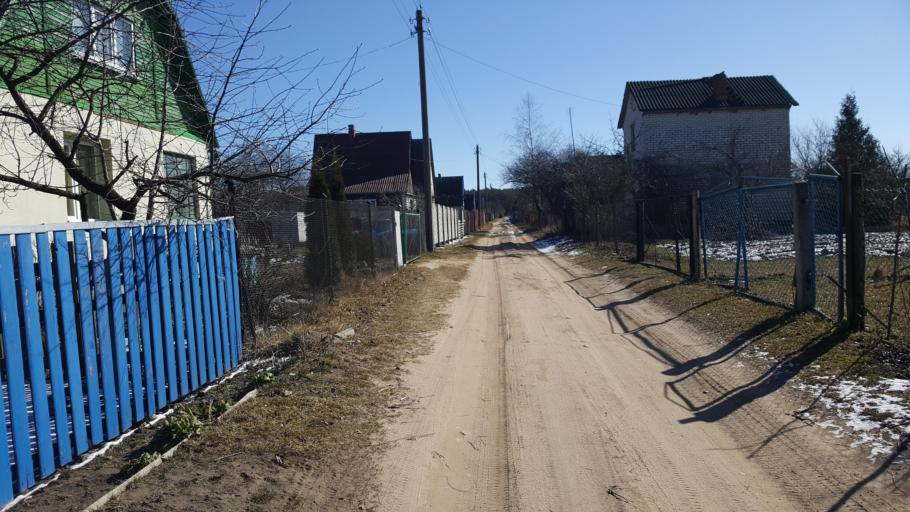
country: BY
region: Brest
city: Kamyanyets
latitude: 52.3684
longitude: 23.8021
